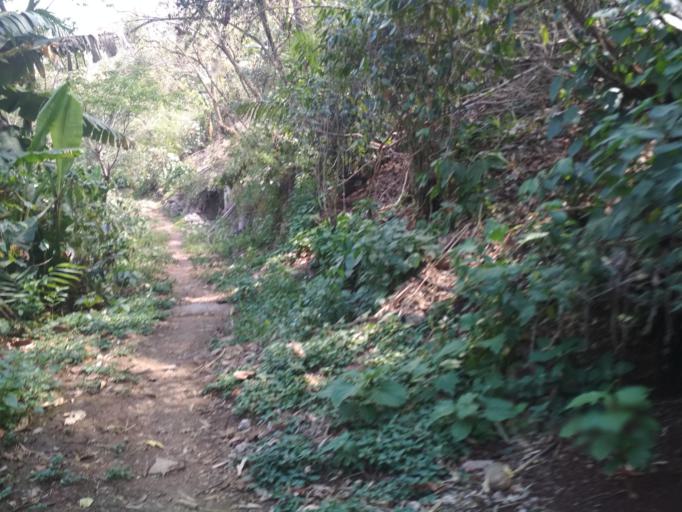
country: MX
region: Veracruz
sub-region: Tlilapan
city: Tonalixco
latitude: 18.7844
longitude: -97.0861
